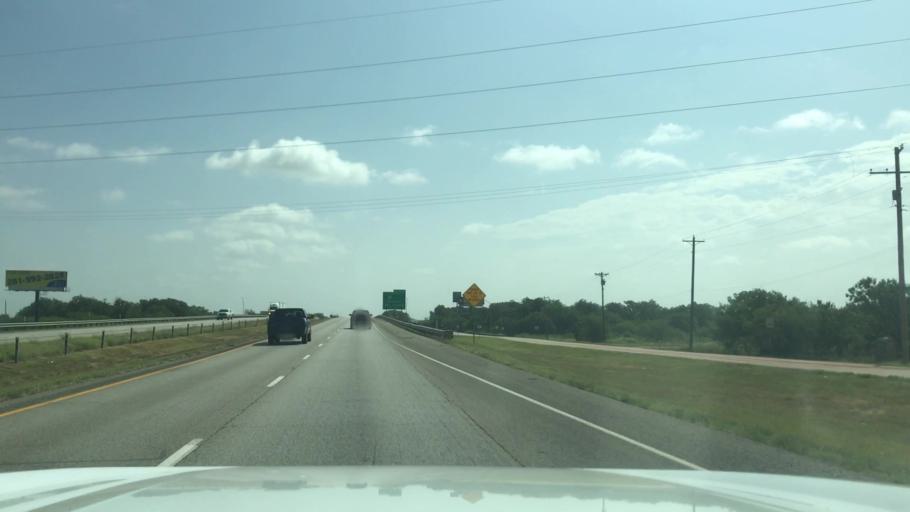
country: US
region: Texas
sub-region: Taylor County
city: Abilene
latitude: 32.4765
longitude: -99.7899
